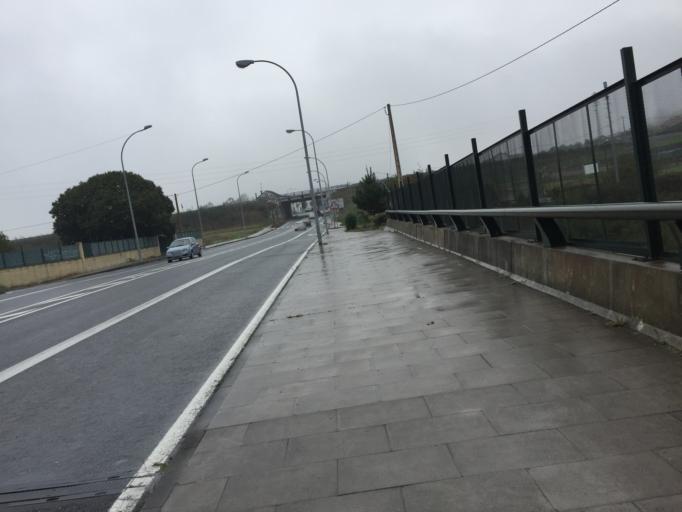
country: ES
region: Galicia
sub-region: Provincia da Coruna
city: Santiago de Compostela
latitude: 42.8550
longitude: -8.5395
